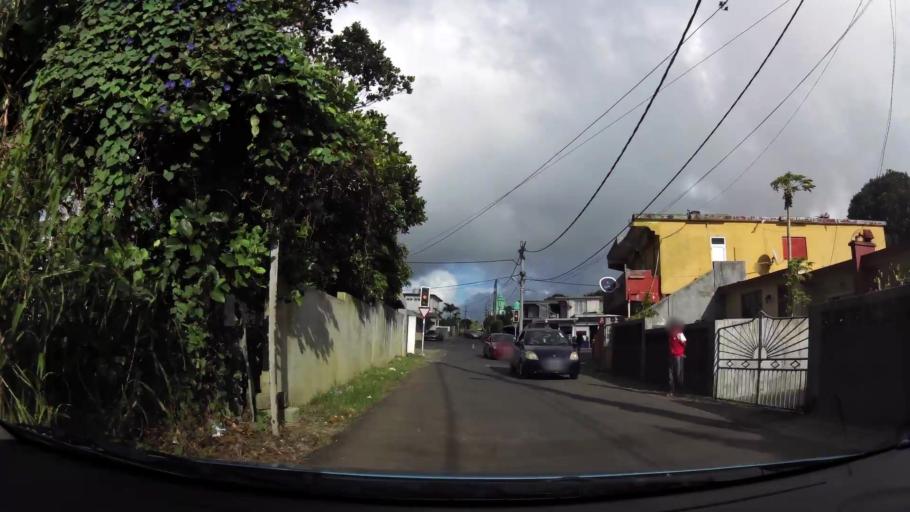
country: MU
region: Plaines Wilhems
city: Curepipe
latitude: -20.3268
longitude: 57.5070
